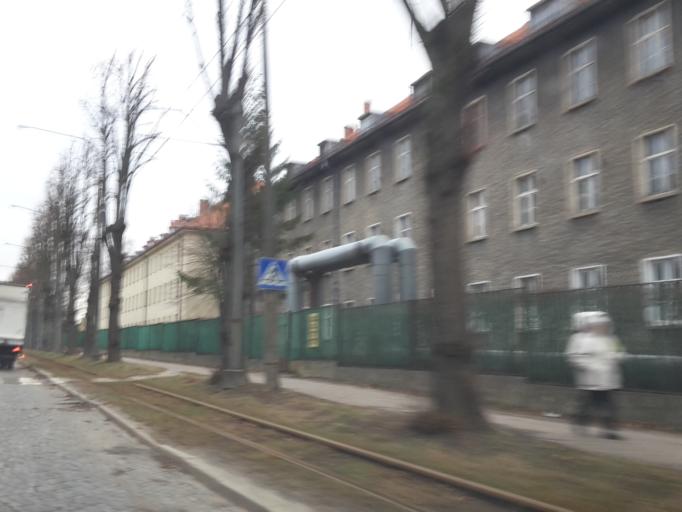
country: PL
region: Warmian-Masurian Voivodeship
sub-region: Powiat elblaski
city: Elblag
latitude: 54.1736
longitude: 19.4162
